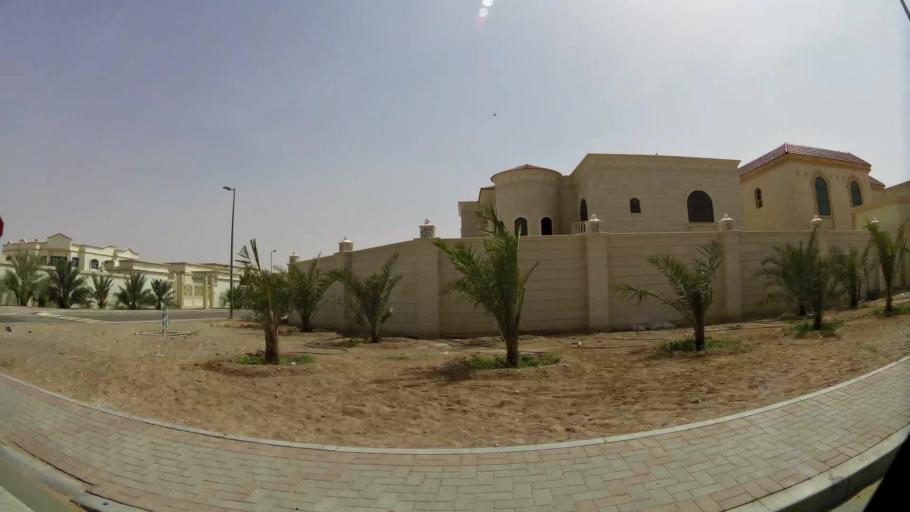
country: AE
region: Abu Dhabi
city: Al Ain
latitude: 24.1634
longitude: 55.6574
